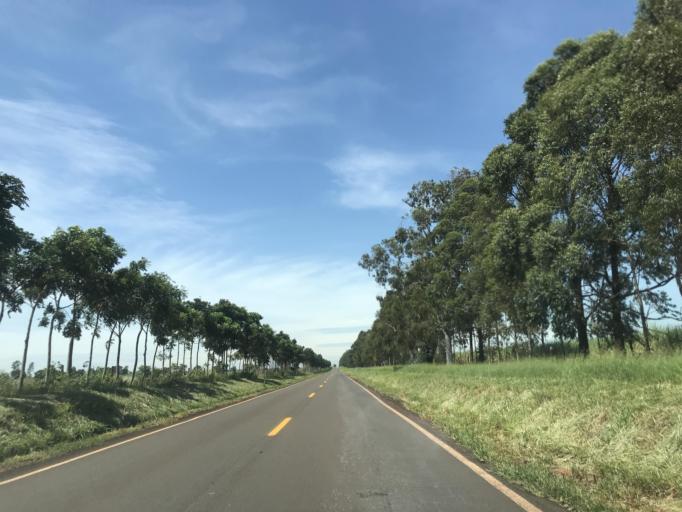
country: BR
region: Parana
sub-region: Paranavai
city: Nova Aurora
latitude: -22.8504
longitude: -52.6577
